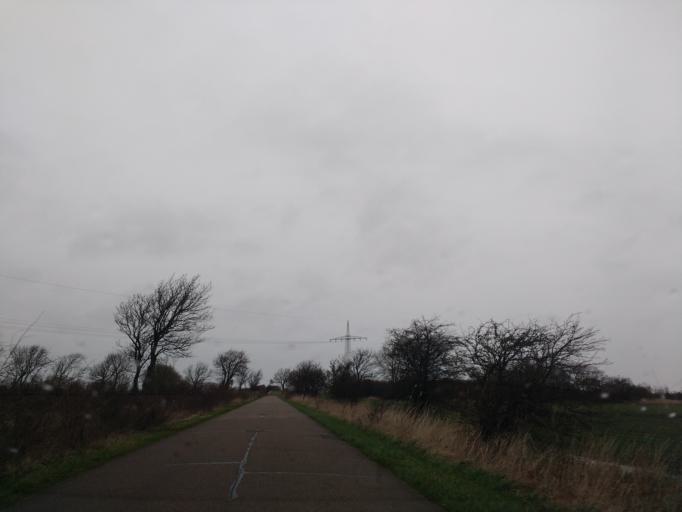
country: DE
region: Schleswig-Holstein
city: Grossenbrode
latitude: 54.3805
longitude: 11.0990
